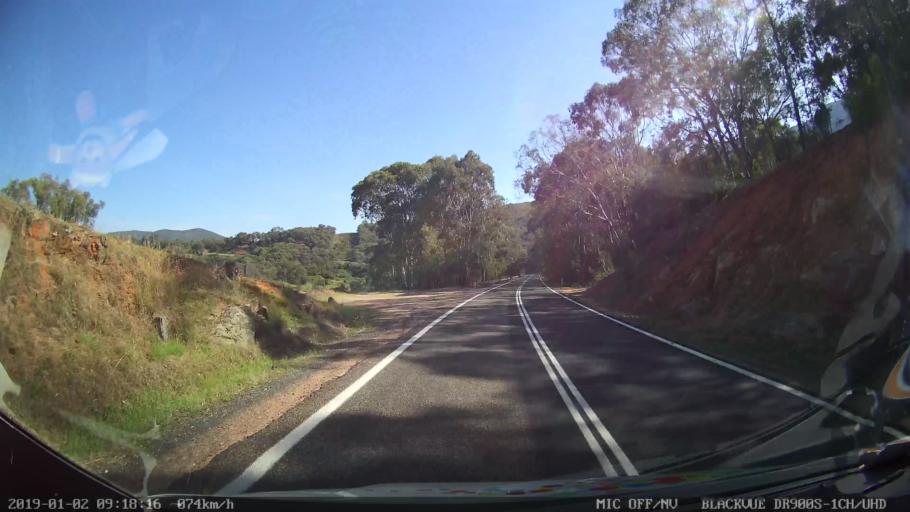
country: AU
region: New South Wales
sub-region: Tumut Shire
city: Tumut
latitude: -35.4307
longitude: 148.2855
